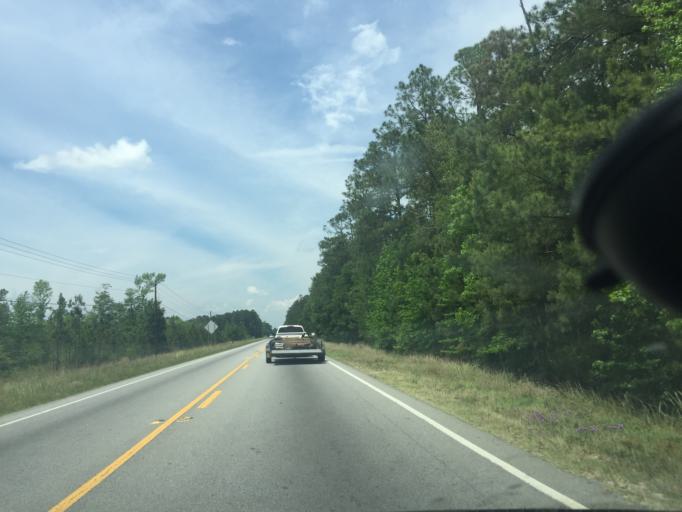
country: US
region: Georgia
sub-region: Chatham County
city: Bloomingdale
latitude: 32.1609
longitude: -81.3700
